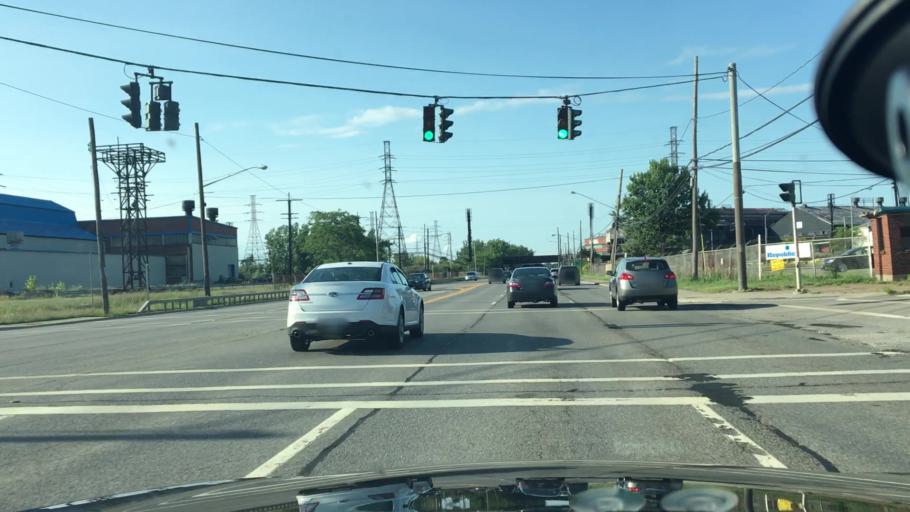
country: US
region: New York
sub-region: Erie County
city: Blasdell
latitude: 42.8013
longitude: -78.8465
